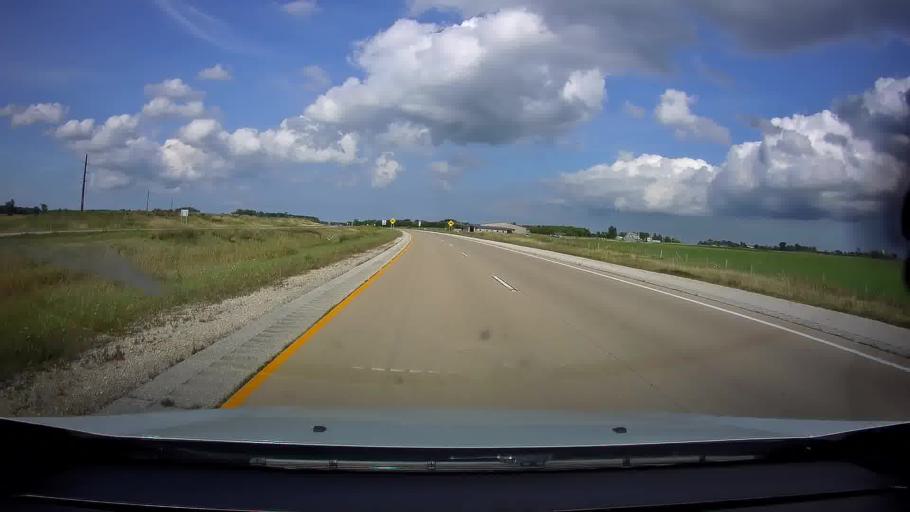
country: US
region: Wisconsin
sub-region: Kewaunee County
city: Luxemburg
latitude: 44.7185
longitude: -87.6168
